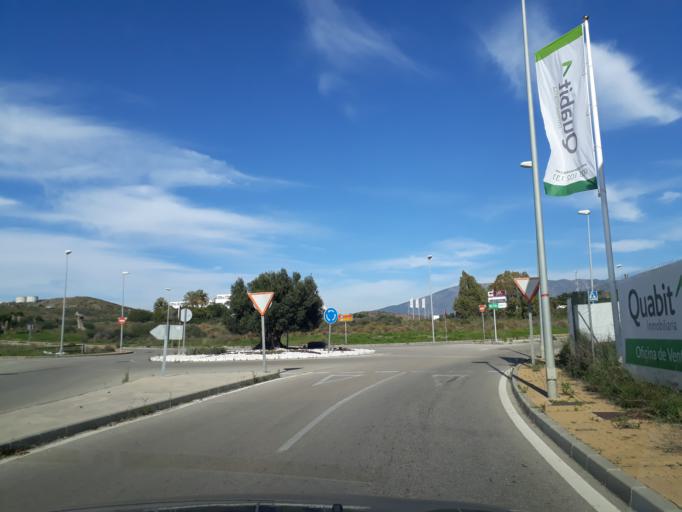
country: ES
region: Andalusia
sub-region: Provincia de Malaga
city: Fuengirola
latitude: 36.5247
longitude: -4.6867
